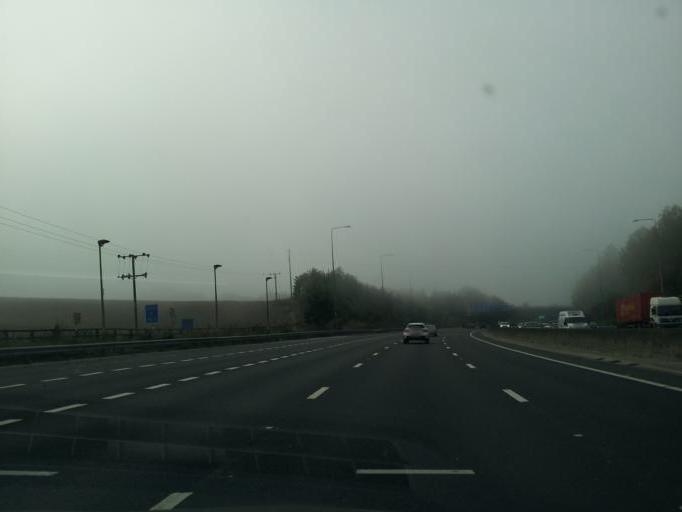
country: GB
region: England
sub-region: Kirklees
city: Cleckheaton
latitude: 53.7046
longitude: -1.7430
